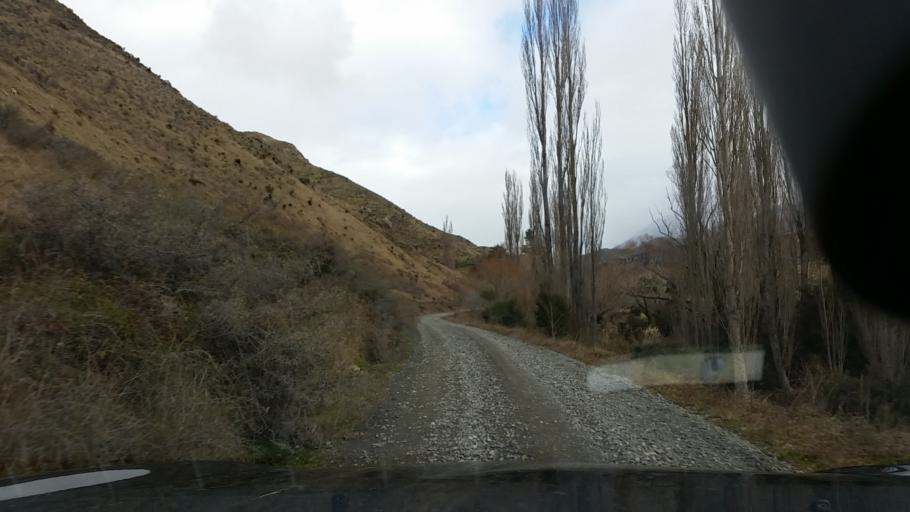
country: NZ
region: Tasman
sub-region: Tasman District
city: Brightwater
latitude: -41.7441
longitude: 173.4137
